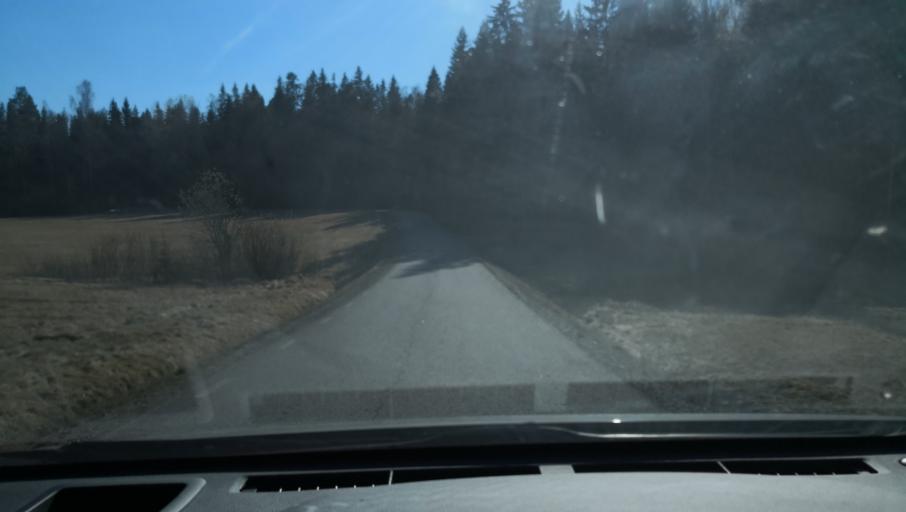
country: SE
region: Dalarna
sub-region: Avesta Kommun
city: Horndal
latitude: 60.0848
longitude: 16.3974
